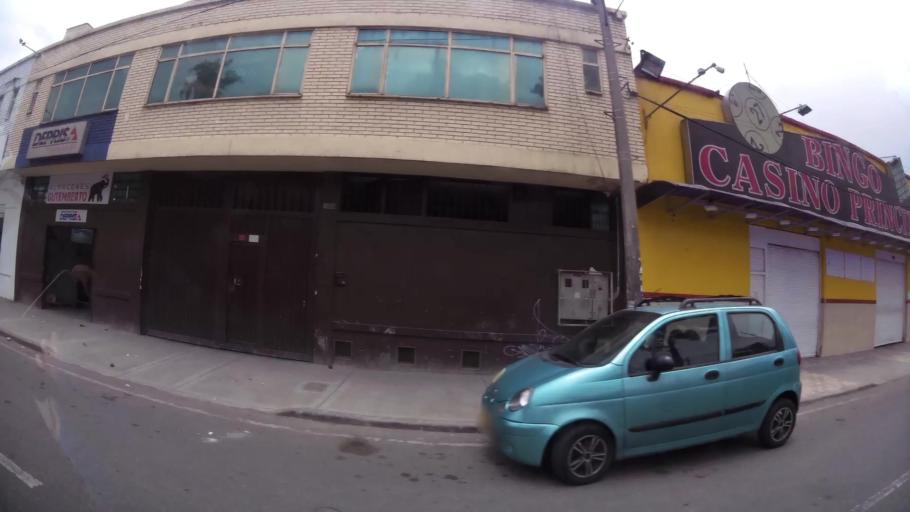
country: CO
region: Bogota D.C.
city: Bogota
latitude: 4.5905
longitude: -74.1079
